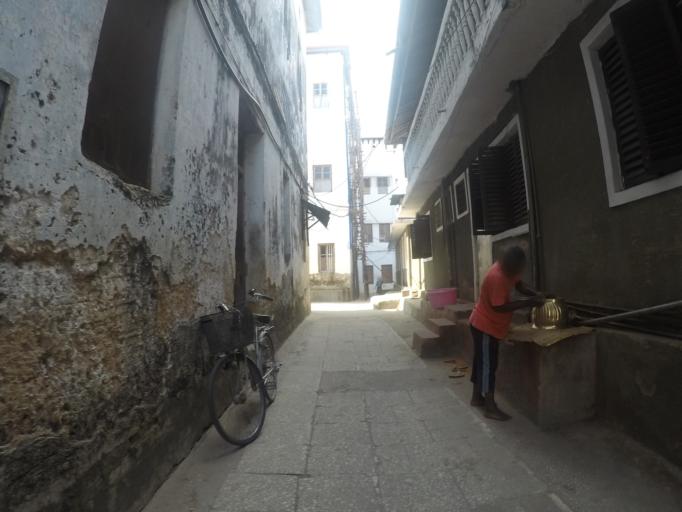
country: TZ
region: Zanzibar Urban/West
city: Zanzibar
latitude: -6.1622
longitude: 39.1911
